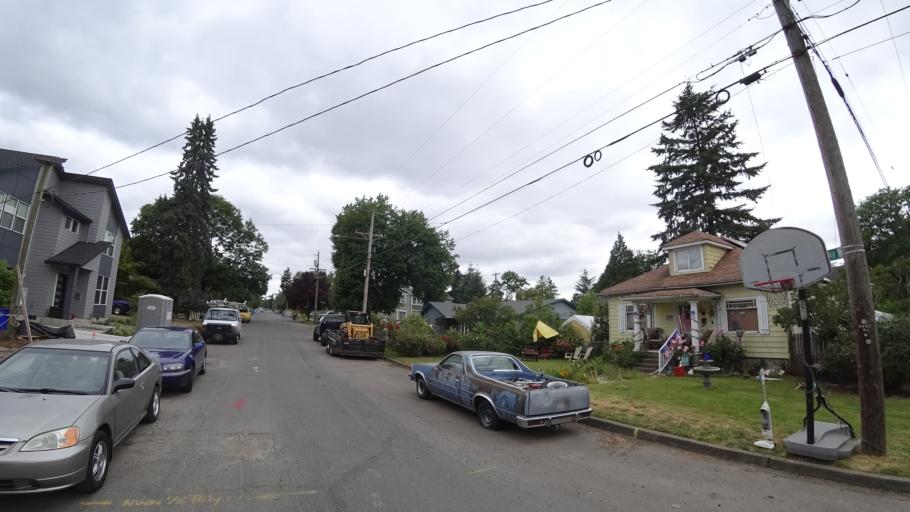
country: US
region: Oregon
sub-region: Multnomah County
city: Lents
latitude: 45.4724
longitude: -122.5856
